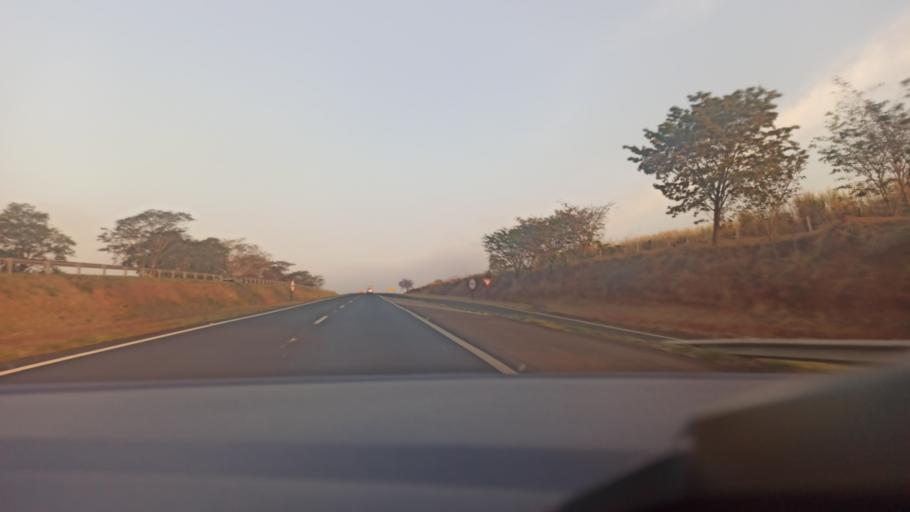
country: BR
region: Sao Paulo
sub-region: Taquaritinga
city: Taquaritinga
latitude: -21.4370
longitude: -48.6546
